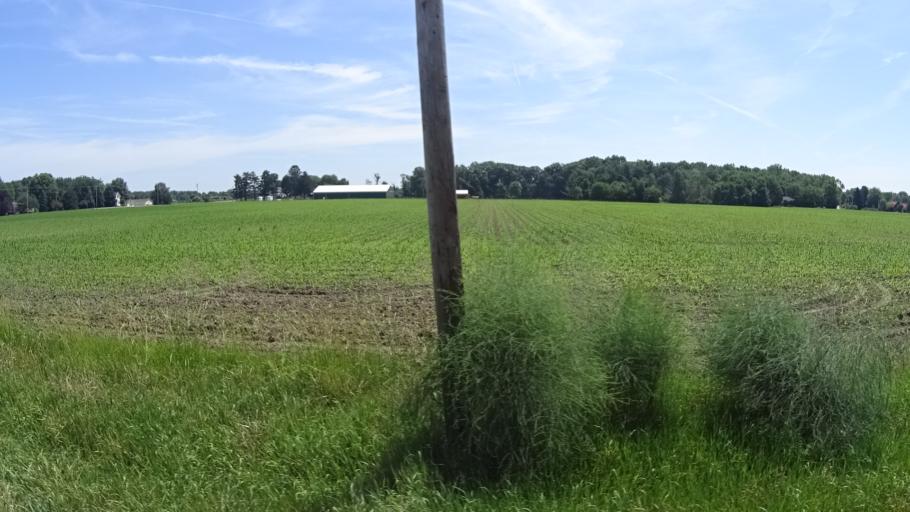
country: US
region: Ohio
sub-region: Erie County
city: Huron
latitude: 41.3631
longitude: -82.4944
